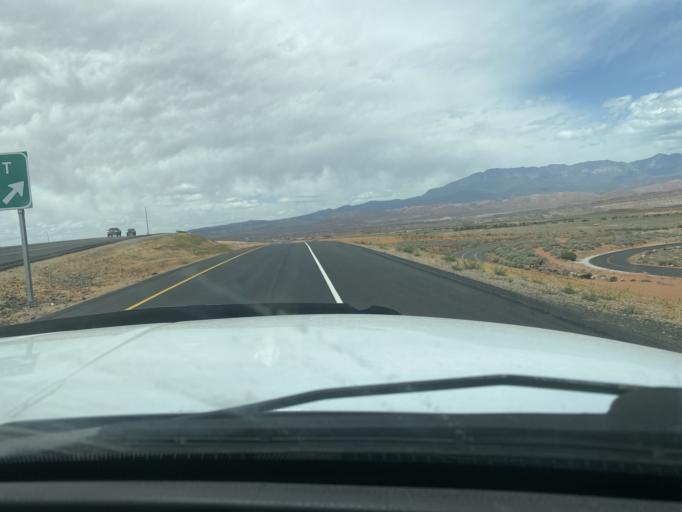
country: US
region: Utah
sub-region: Washington County
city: Washington
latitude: 37.1050
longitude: -113.3942
